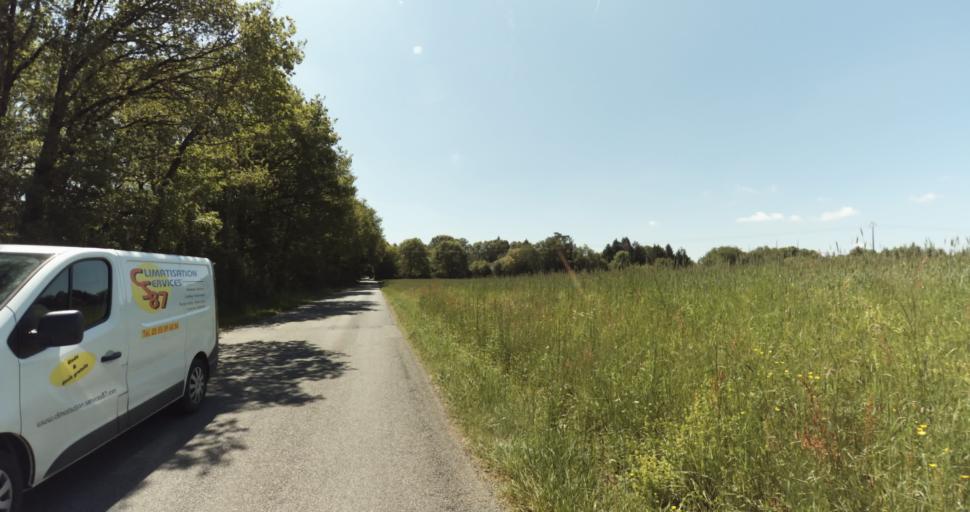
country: FR
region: Limousin
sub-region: Departement de la Haute-Vienne
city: Condat-sur-Vienne
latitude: 45.7848
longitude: 1.3007
